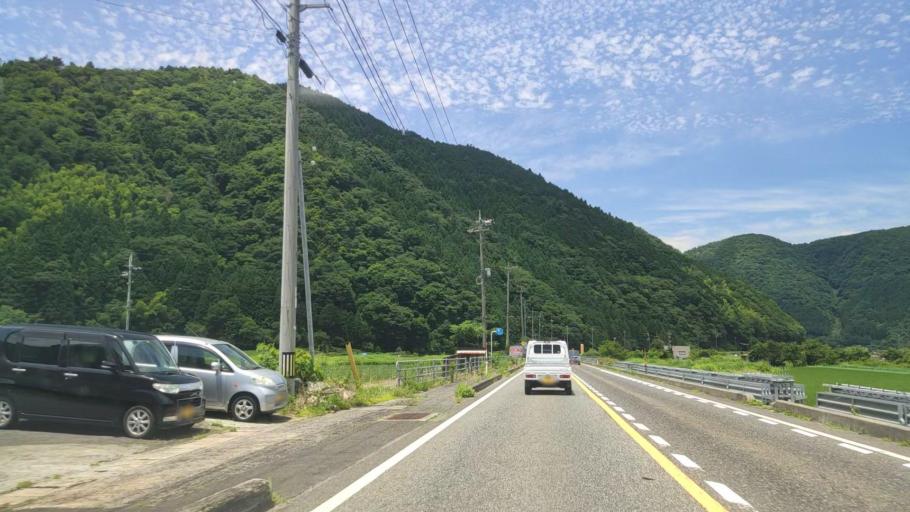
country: JP
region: Tottori
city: Tottori
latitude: 35.3584
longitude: 134.3802
